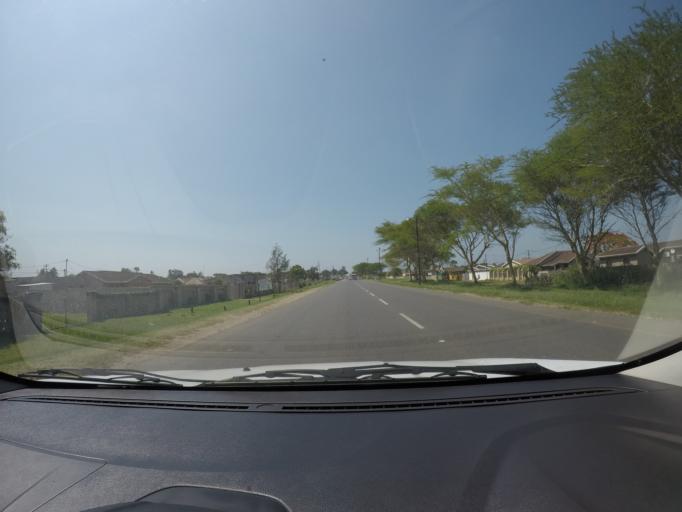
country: ZA
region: KwaZulu-Natal
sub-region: uThungulu District Municipality
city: eSikhawini
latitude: -28.8609
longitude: 31.9245
